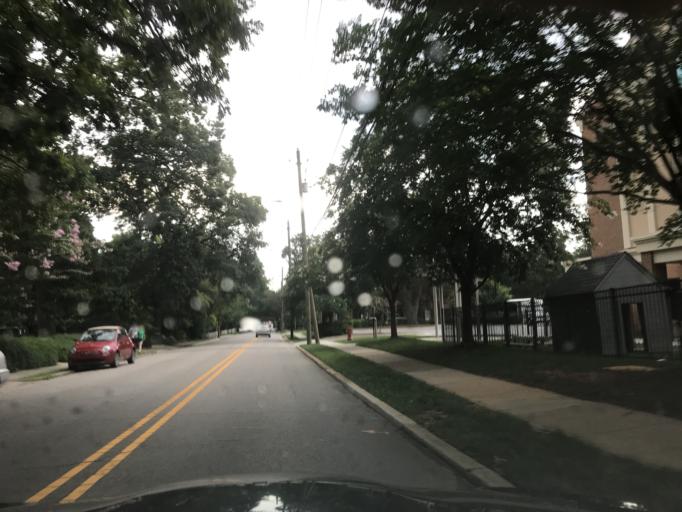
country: US
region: North Carolina
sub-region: Wake County
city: West Raleigh
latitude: 35.8072
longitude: -78.6509
